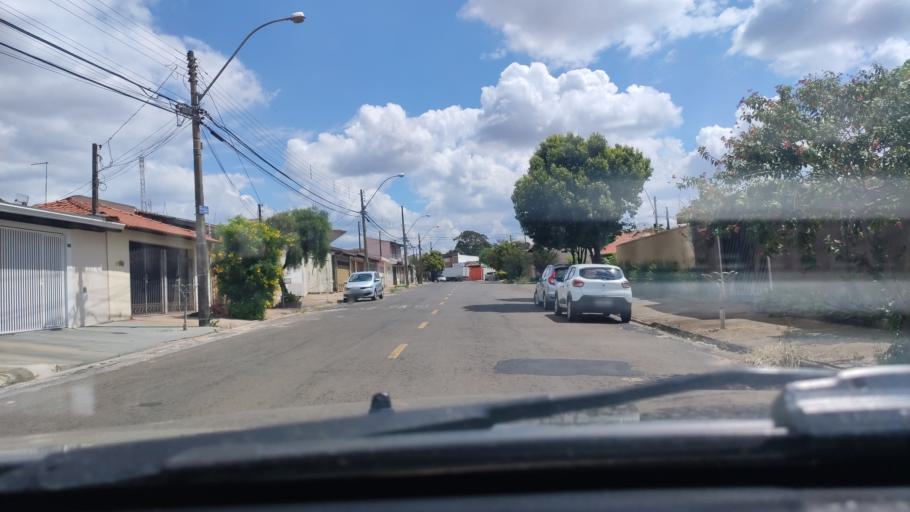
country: BR
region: Sao Paulo
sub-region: Sao Carlos
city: Sao Carlos
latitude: -22.0096
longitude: -47.8672
